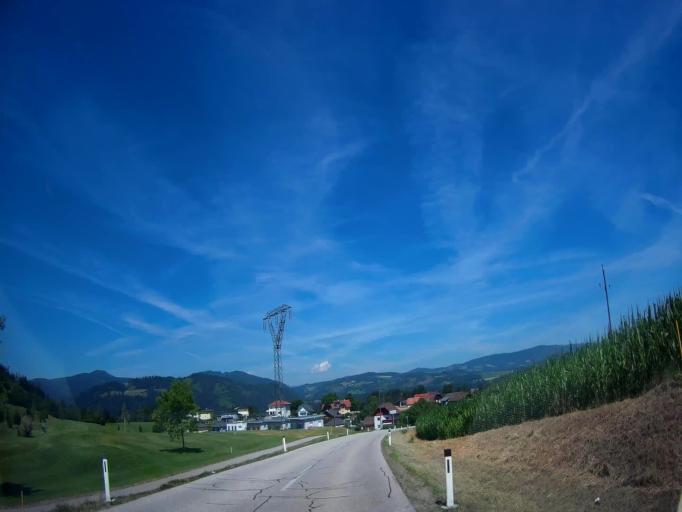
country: AT
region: Carinthia
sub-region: Politischer Bezirk Sankt Veit an der Glan
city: St. Georgen am Laengsee
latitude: 46.7975
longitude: 14.4147
